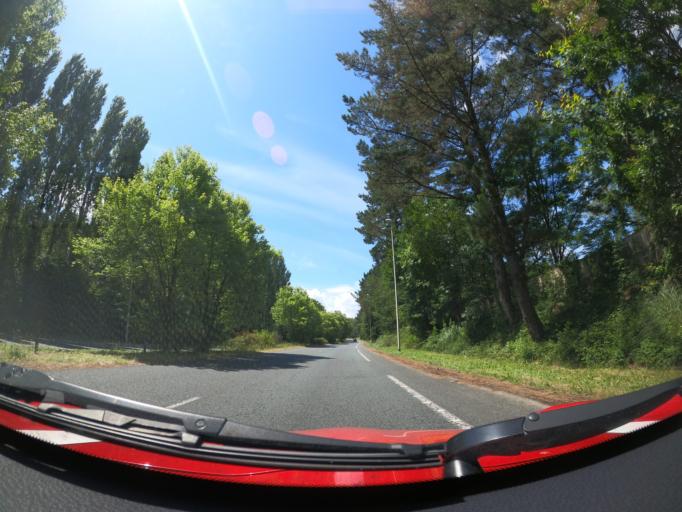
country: FR
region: Aquitaine
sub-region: Departement des Pyrenees-Atlantiques
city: Bayonne
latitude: 43.4719
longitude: -1.4908
